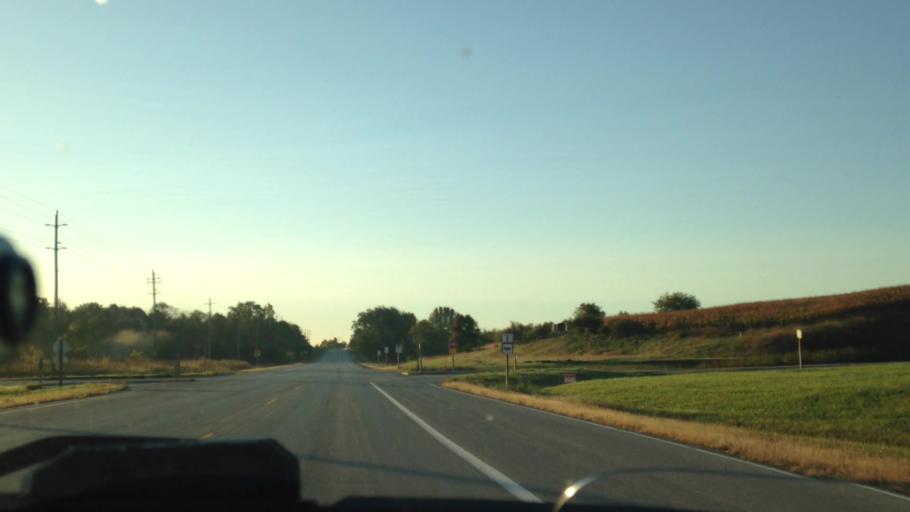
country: US
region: Wisconsin
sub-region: Ozaukee County
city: Saukville
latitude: 43.3963
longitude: -87.9801
